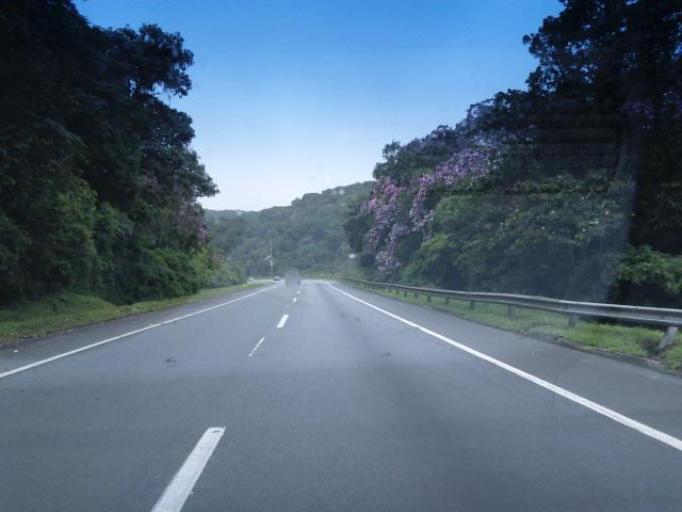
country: BR
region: Sao Paulo
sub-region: Cajati
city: Cajati
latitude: -24.9683
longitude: -48.4466
